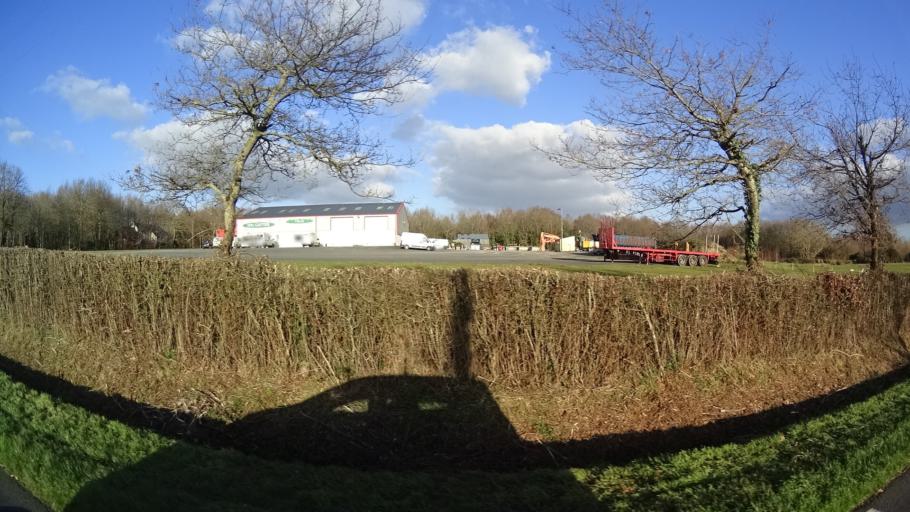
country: FR
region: Pays de la Loire
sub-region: Departement de la Loire-Atlantique
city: Guenrouet
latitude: 47.5356
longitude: -1.9235
